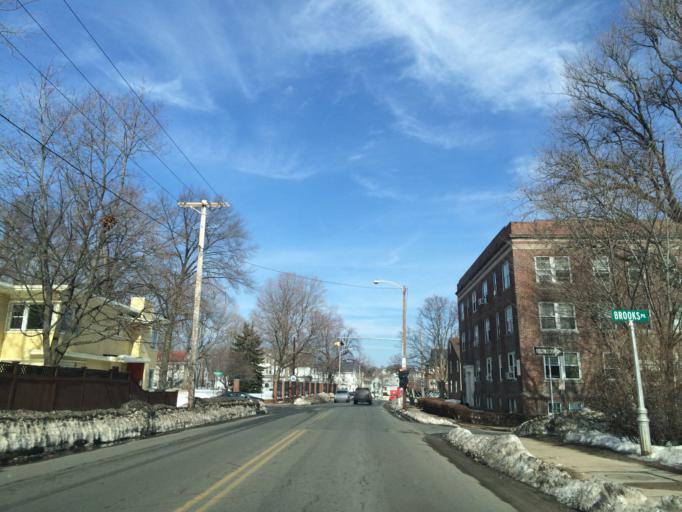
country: US
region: Massachusetts
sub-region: Middlesex County
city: Medford
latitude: 42.4116
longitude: -71.1105
